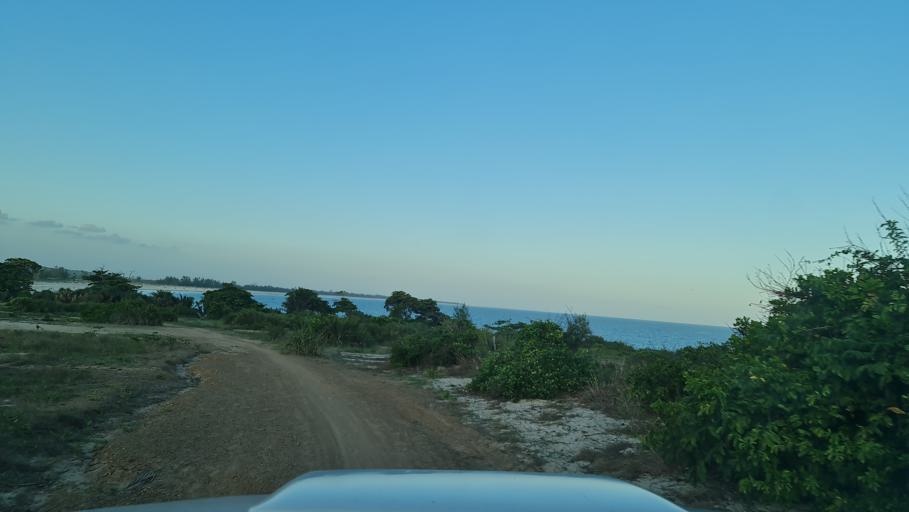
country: MZ
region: Nampula
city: Ilha de Mocambique
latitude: -15.6286
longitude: 40.4220
